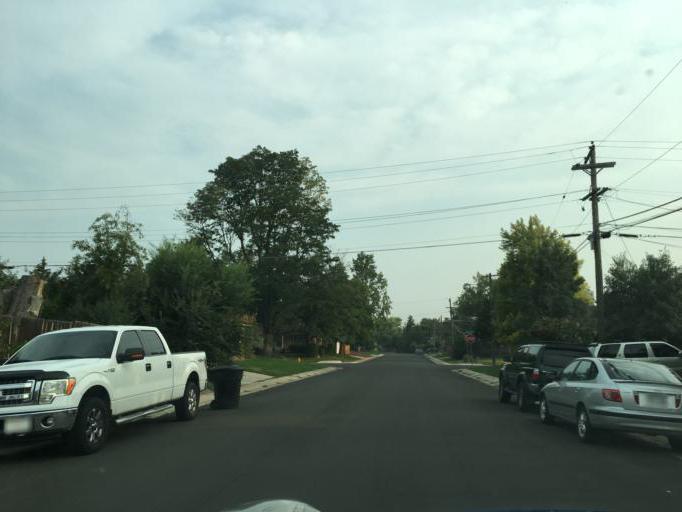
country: US
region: Colorado
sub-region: Arapahoe County
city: Glendale
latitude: 39.6856
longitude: -104.9349
